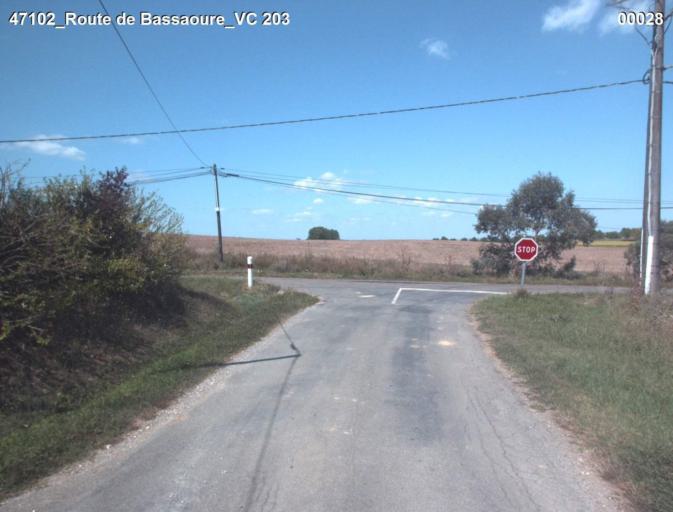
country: FR
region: Aquitaine
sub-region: Departement du Lot-et-Garonne
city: Nerac
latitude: 44.0575
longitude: 0.4229
